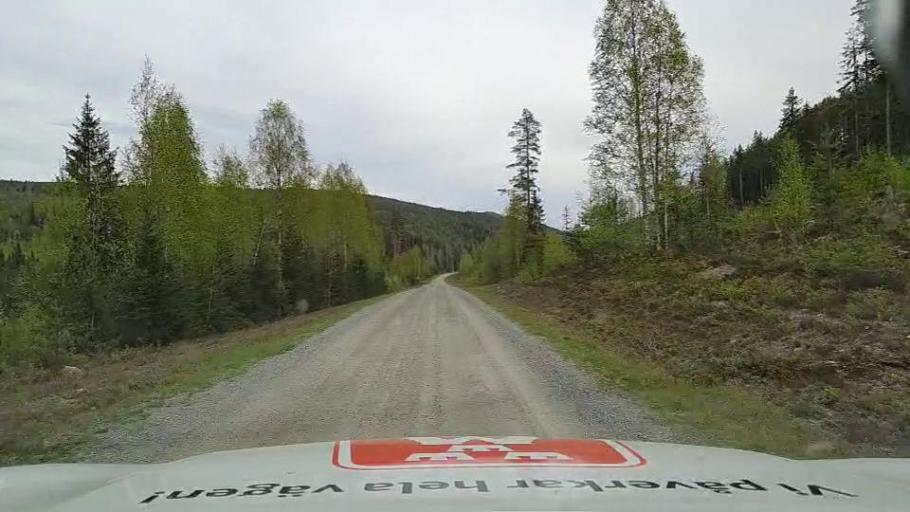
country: SE
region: Jaemtland
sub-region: Bergs Kommun
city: Hoverberg
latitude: 62.5311
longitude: 14.7081
